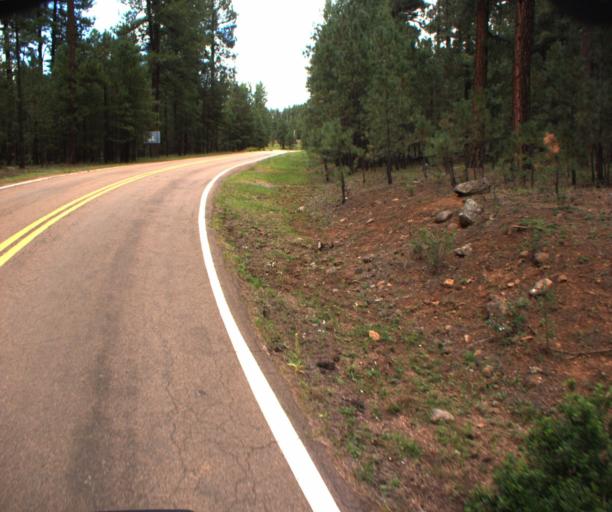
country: US
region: Arizona
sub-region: Navajo County
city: Pinetop-Lakeside
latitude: 34.0482
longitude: -109.7300
